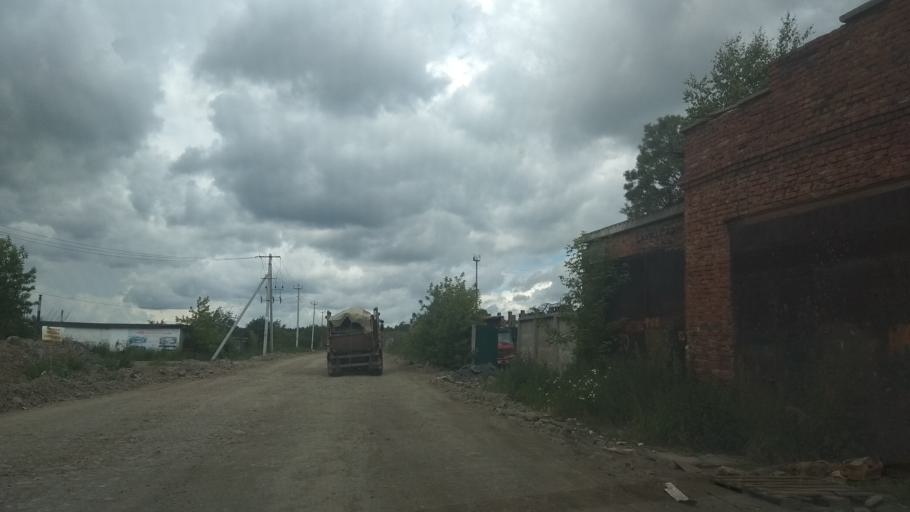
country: RU
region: Sverdlovsk
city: Verkhnyaya Pyshma
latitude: 56.9168
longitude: 60.5735
